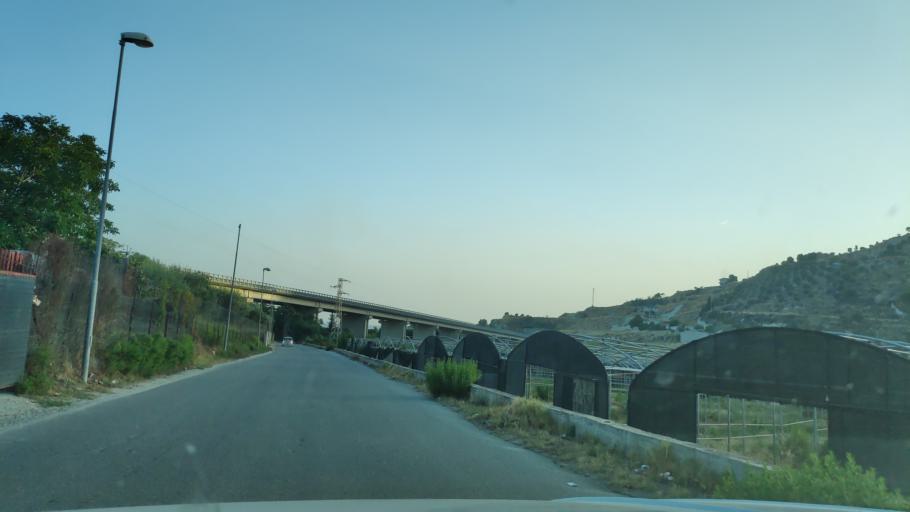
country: IT
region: Calabria
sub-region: Provincia di Reggio Calabria
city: Bova Marina
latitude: 37.9346
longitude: 15.9118
